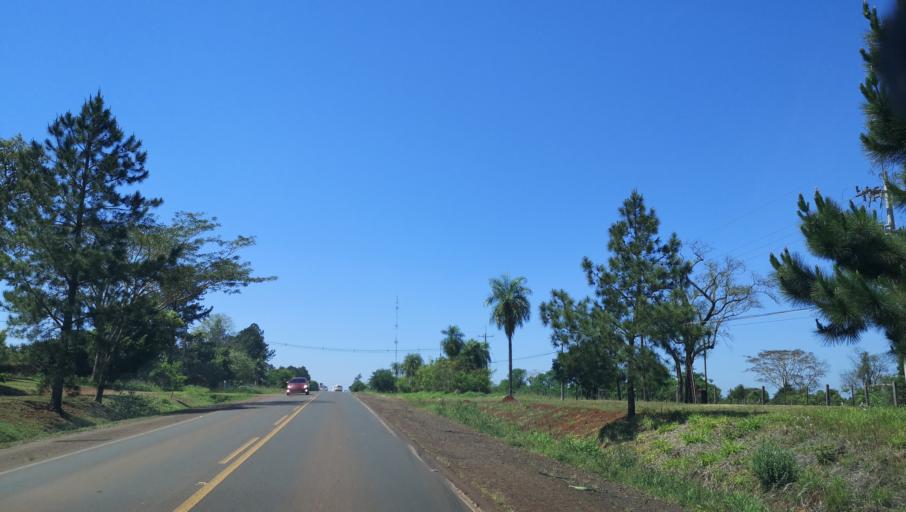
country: PY
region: Itapua
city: San Juan del Parana
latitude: -27.2618
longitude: -55.9642
